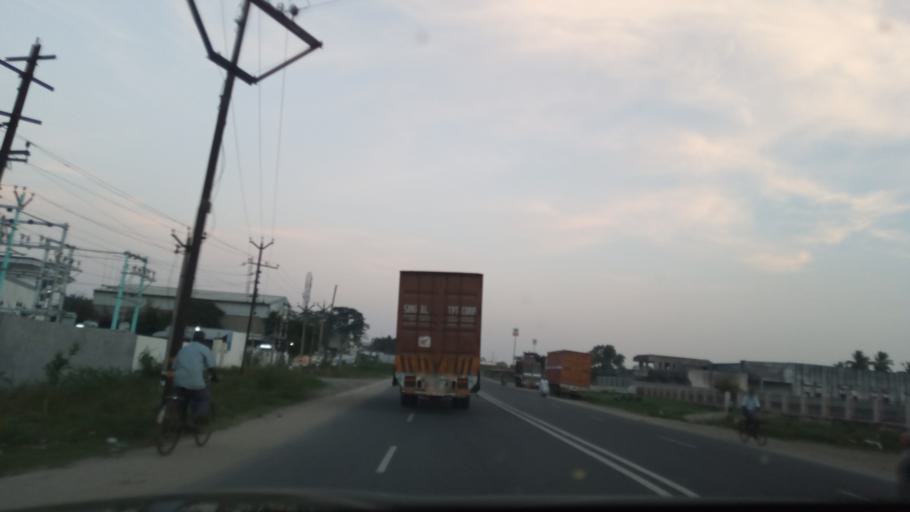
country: IN
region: Tamil Nadu
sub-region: Vellore
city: Walajapet
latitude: 12.9282
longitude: 79.3454
